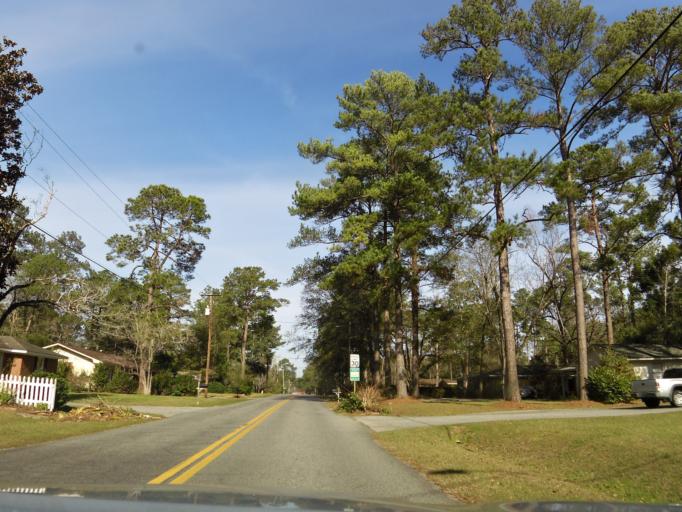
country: US
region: Georgia
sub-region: Lowndes County
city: Remerton
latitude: 30.8554
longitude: -83.2994
